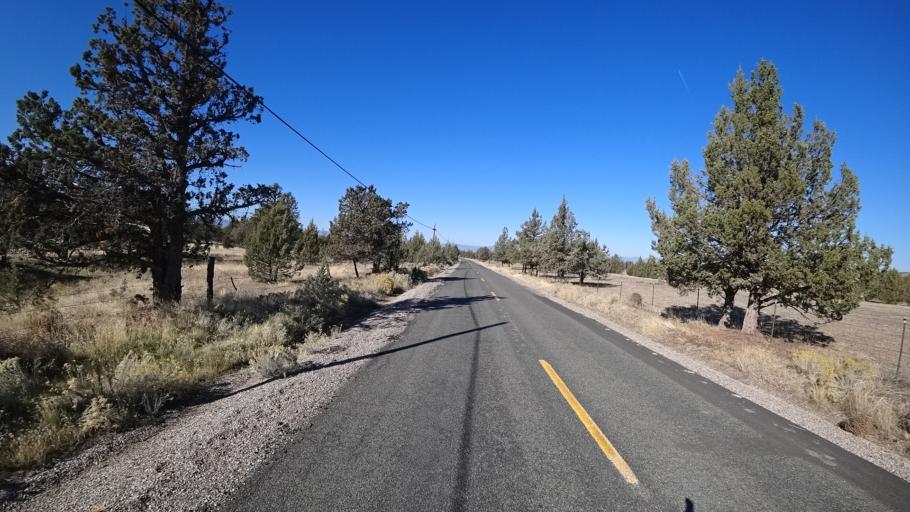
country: US
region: California
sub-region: Siskiyou County
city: Montague
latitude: 41.6417
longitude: -122.3469
